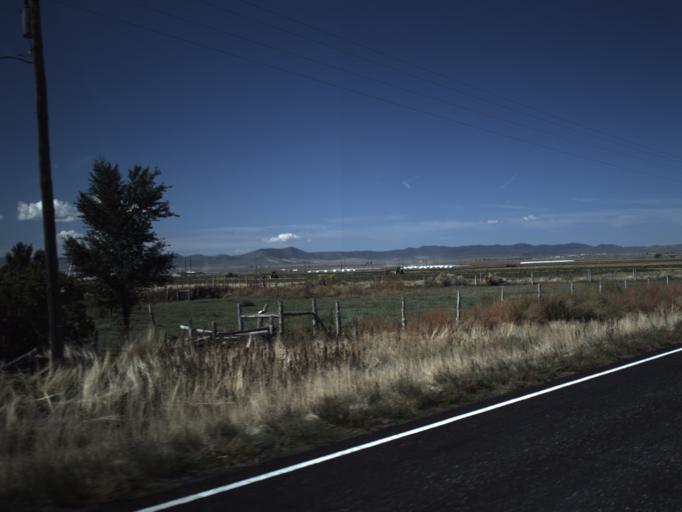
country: US
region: Utah
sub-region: Washington County
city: Enterprise
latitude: 37.6751
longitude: -113.5608
